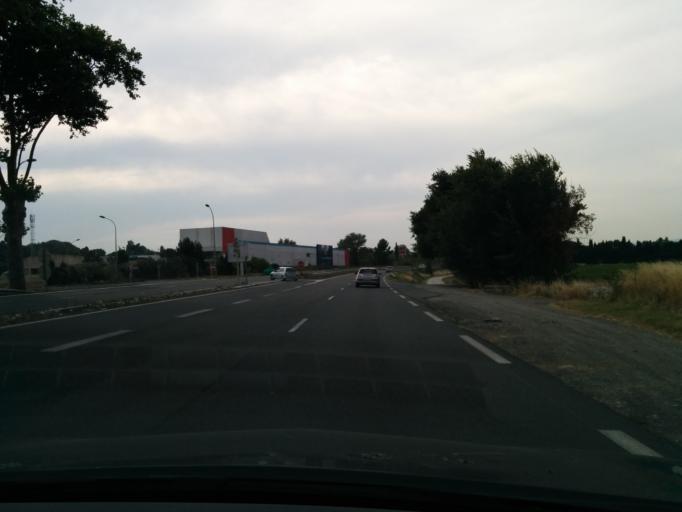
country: FR
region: Languedoc-Roussillon
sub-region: Departement de l'Aude
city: Pennautier
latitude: 43.2315
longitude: 2.3235
